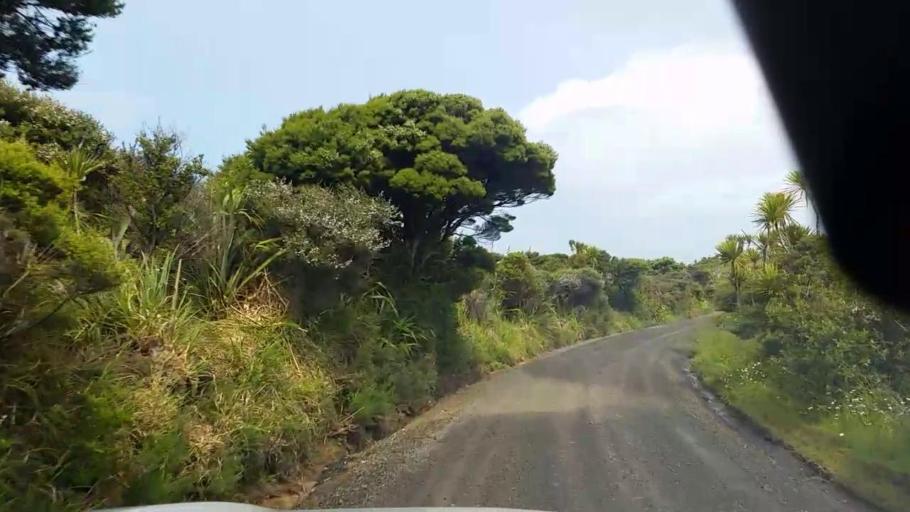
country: NZ
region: Auckland
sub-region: Auckland
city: Muriwai Beach
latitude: -36.9320
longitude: 174.4640
